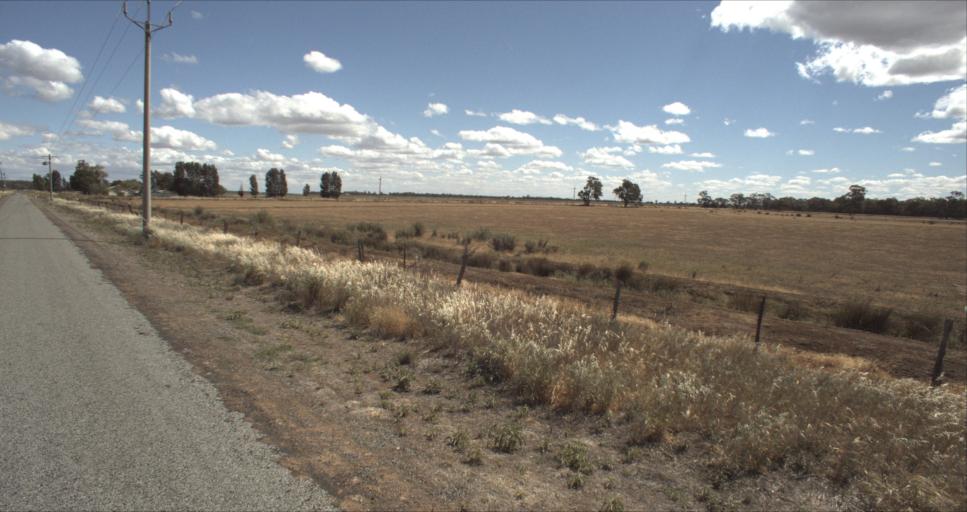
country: AU
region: New South Wales
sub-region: Leeton
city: Leeton
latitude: -34.5230
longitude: 146.2228
